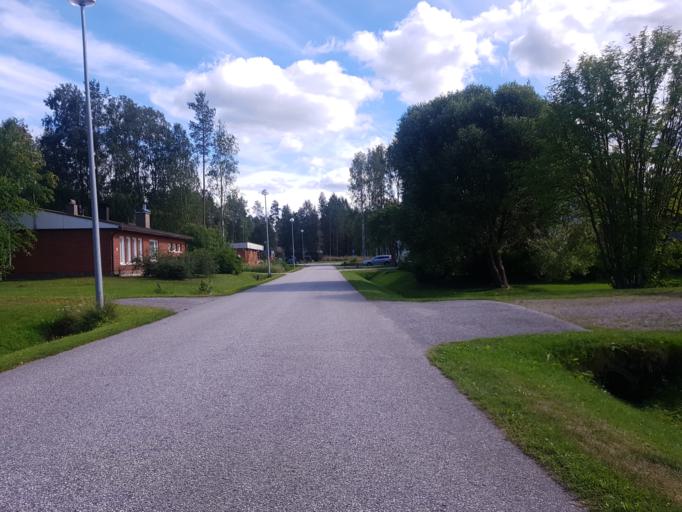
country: FI
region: Kainuu
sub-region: Kehys-Kainuu
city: Kuhmo
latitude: 64.1226
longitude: 29.5273
